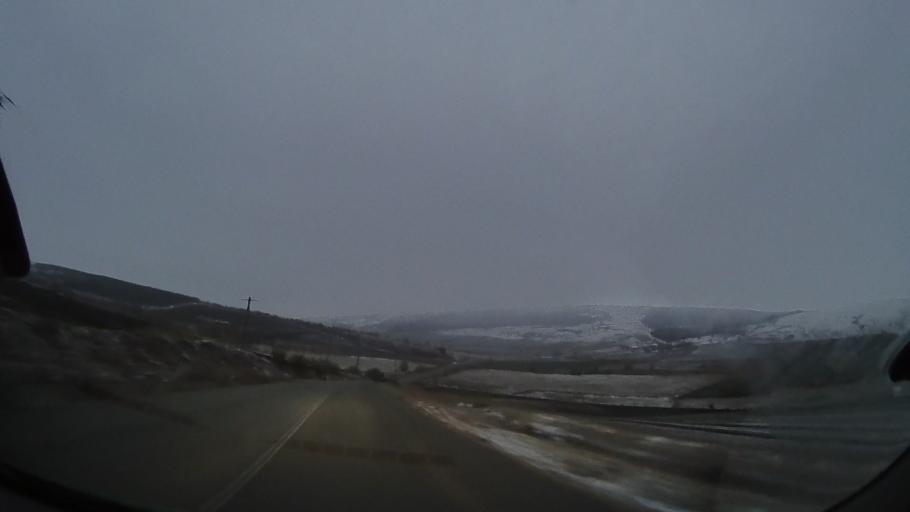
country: RO
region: Vaslui
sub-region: Comuna Vutcani
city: Vutcani
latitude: 46.4030
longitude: 27.9869
